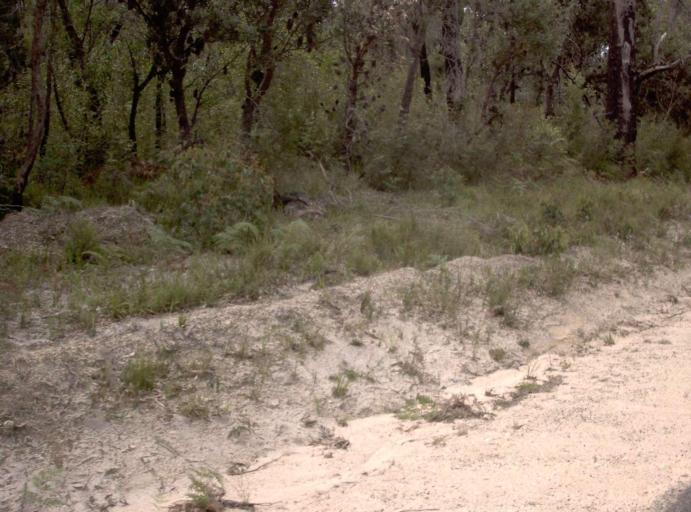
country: AU
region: New South Wales
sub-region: Bega Valley
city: Eden
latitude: -37.4173
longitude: 149.6522
